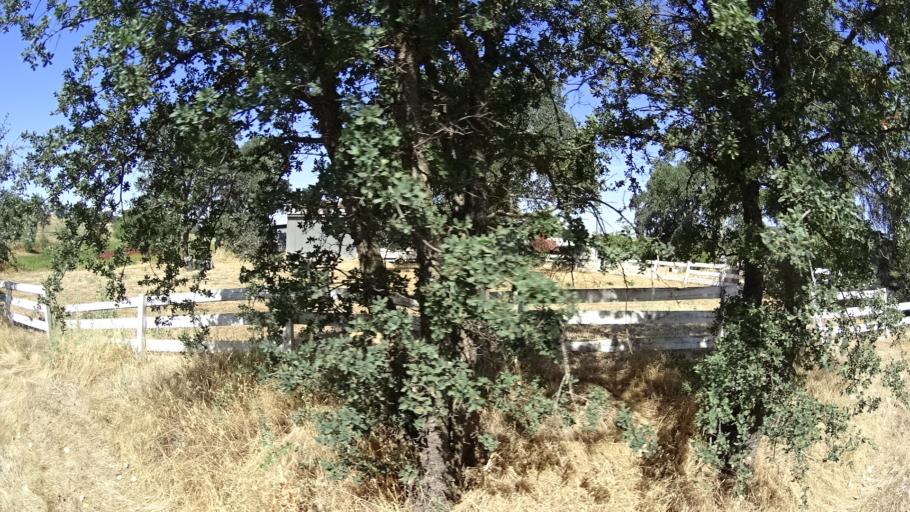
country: US
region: California
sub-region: Calaveras County
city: Rancho Calaveras
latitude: 38.1006
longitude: -120.9265
